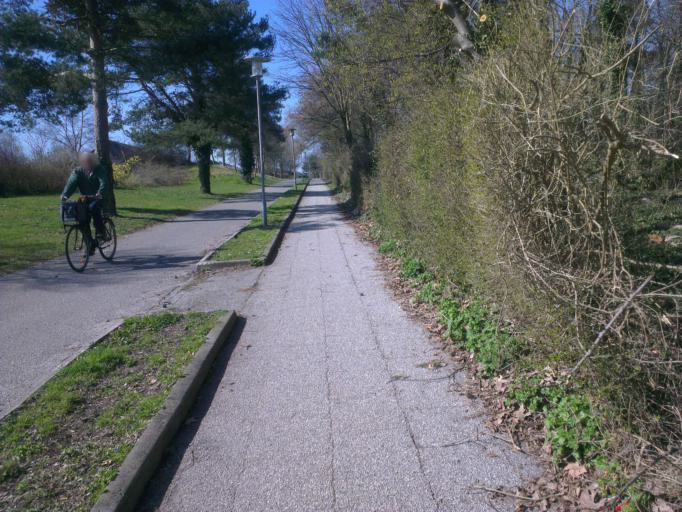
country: DK
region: Capital Region
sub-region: Frederikssund Kommune
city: Frederikssund
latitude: 55.8481
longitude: 12.0562
